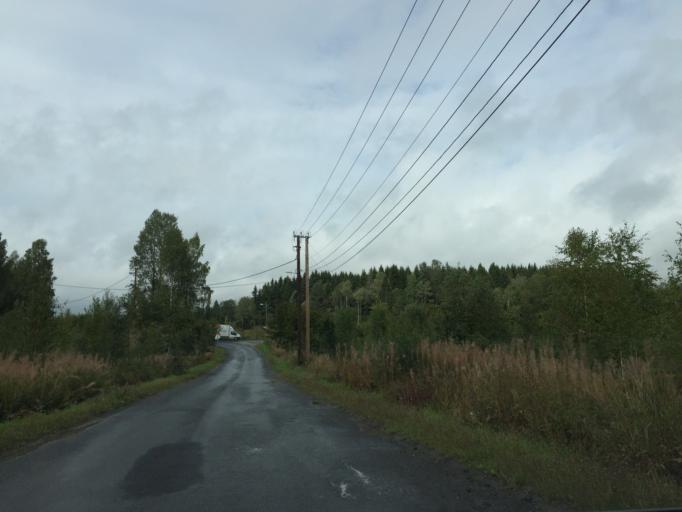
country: NO
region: Akershus
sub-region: Baerum
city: Lysaker
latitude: 60.0184
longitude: 10.6183
